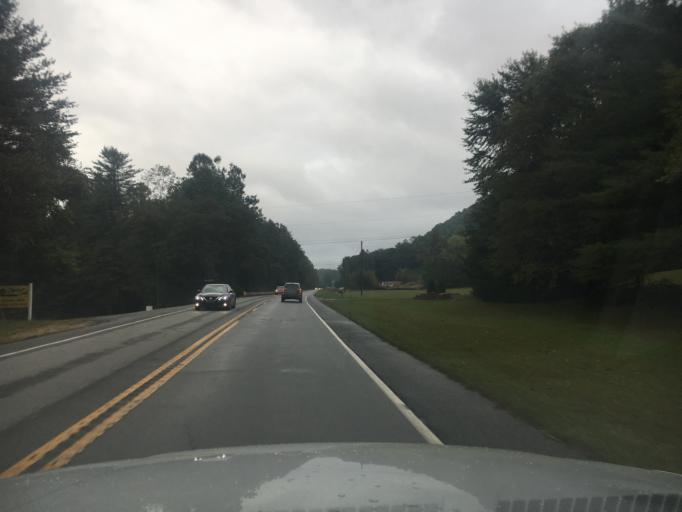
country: US
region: North Carolina
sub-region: Henderson County
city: Horse Shoe
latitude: 35.3310
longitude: -82.5728
